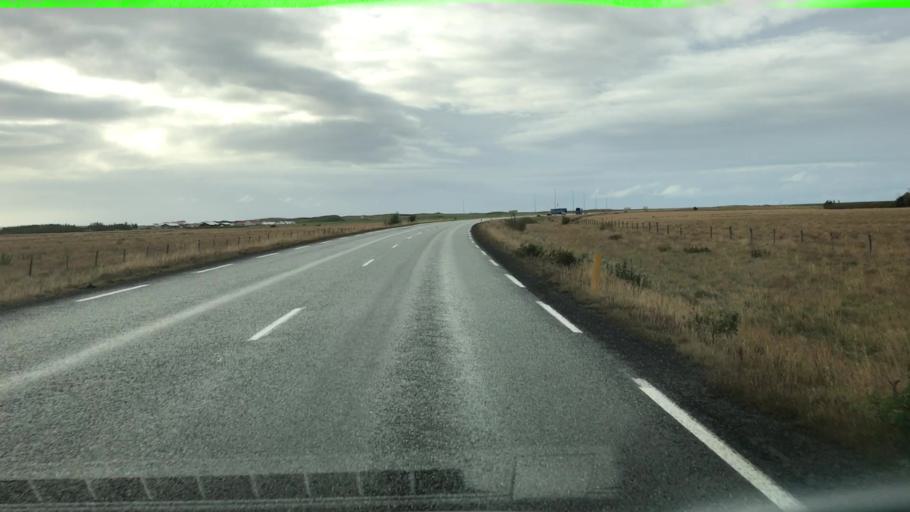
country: IS
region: West
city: Akranes
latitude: 64.3091
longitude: -21.9800
